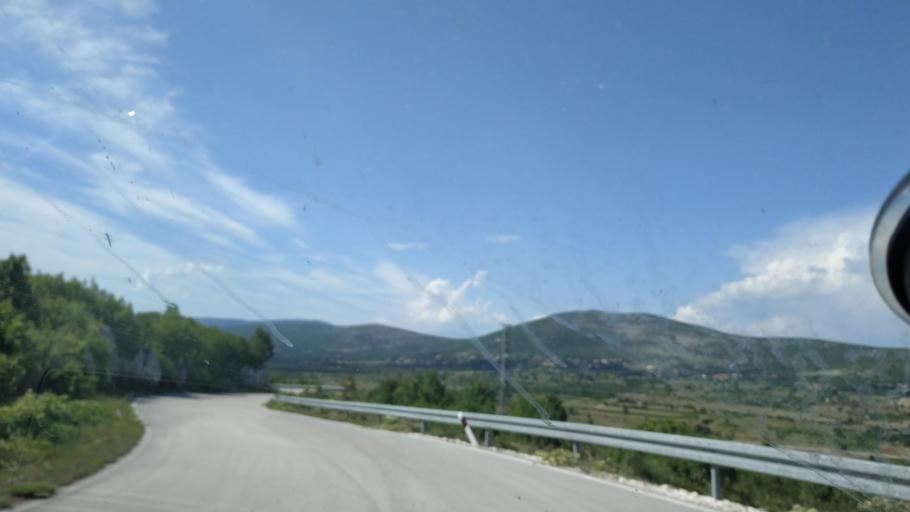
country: HR
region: Splitsko-Dalmatinska
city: Greda
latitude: 43.5827
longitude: 16.6541
